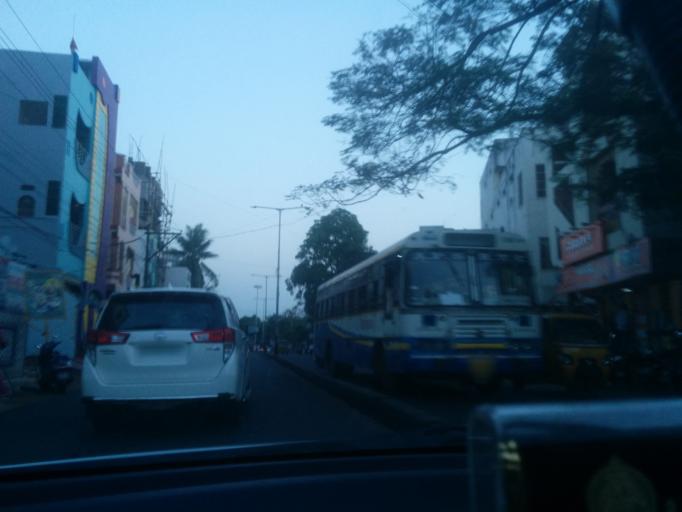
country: IN
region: Andhra Pradesh
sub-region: East Godavari
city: Rajahmundry
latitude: 17.0082
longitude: 81.7802
